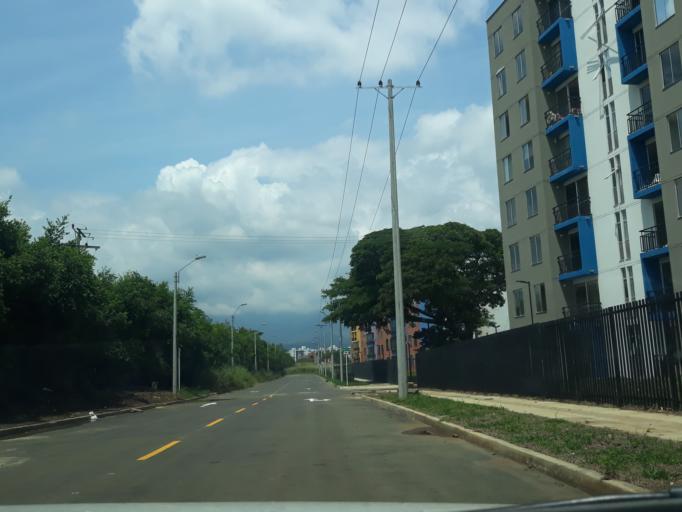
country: CO
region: Valle del Cauca
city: Cali
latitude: 3.3781
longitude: -76.5090
